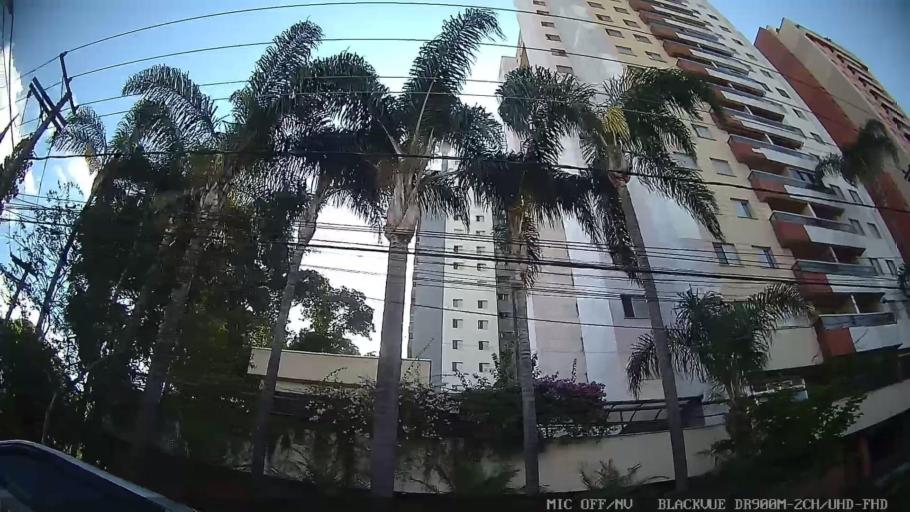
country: BR
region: Sao Paulo
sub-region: Sao Paulo
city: Sao Paulo
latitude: -23.5795
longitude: -46.6048
